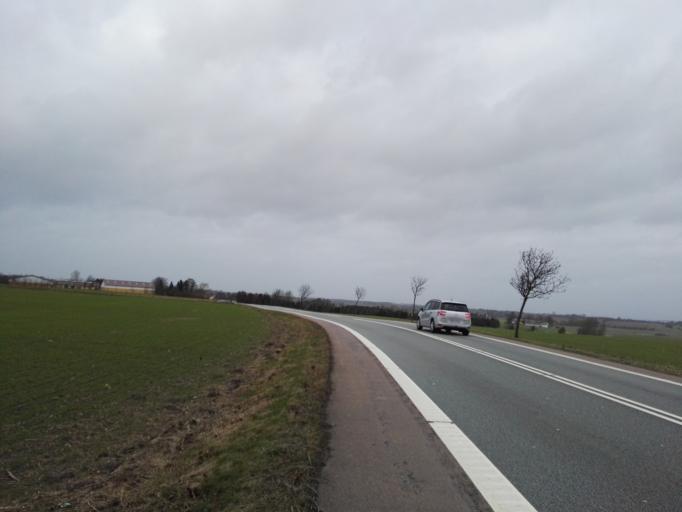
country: DK
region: Capital Region
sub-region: Frederikssund Kommune
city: Skibby
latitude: 55.6764
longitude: 11.9317
